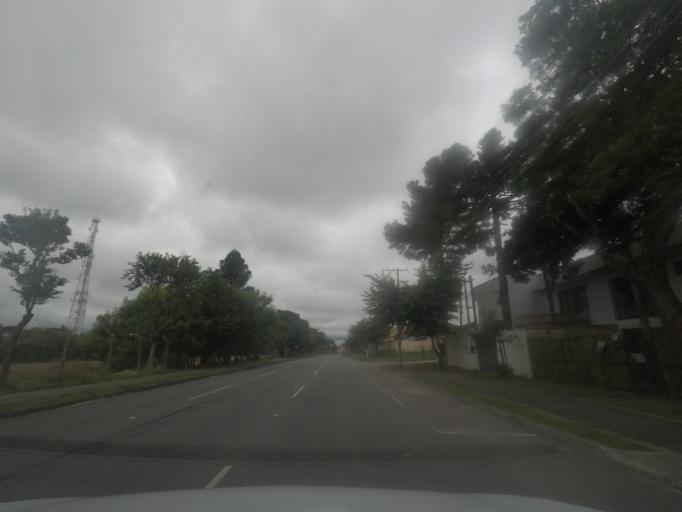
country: BR
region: Parana
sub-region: Pinhais
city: Pinhais
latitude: -25.4406
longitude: -49.2277
